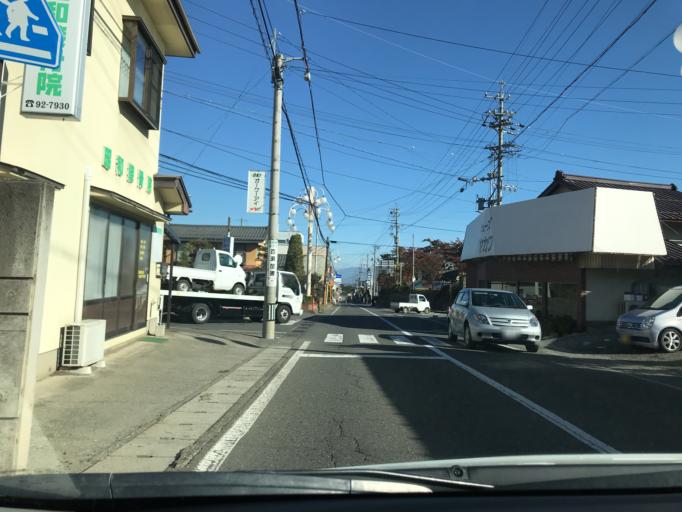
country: JP
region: Nagano
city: Toyoshina
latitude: 36.1961
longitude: 137.8546
